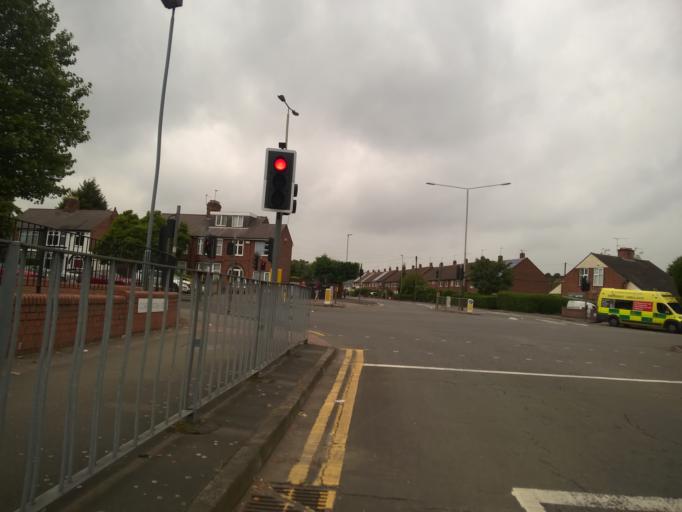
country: GB
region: England
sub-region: City of Leicester
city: Leicester
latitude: 52.6563
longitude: -1.1349
